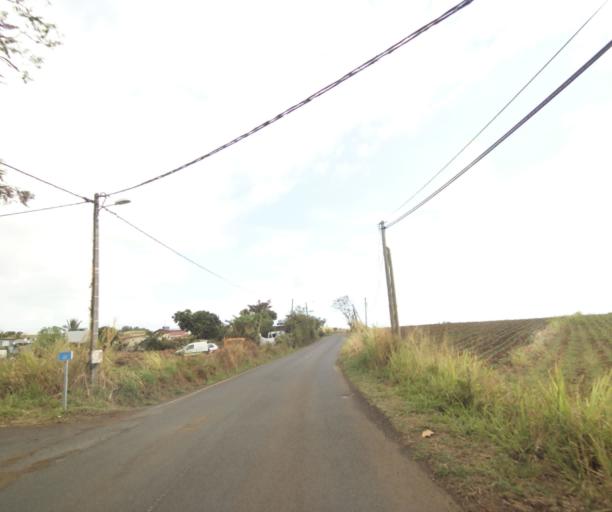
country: RE
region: Reunion
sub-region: Reunion
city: Trois-Bassins
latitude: -21.0691
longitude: 55.2779
